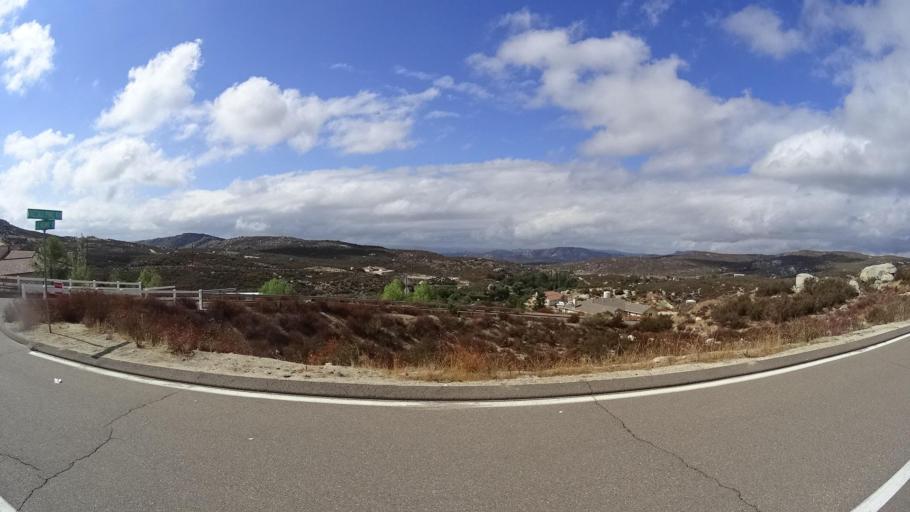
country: US
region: California
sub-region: San Diego County
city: Campo
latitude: 32.7068
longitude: -116.3802
